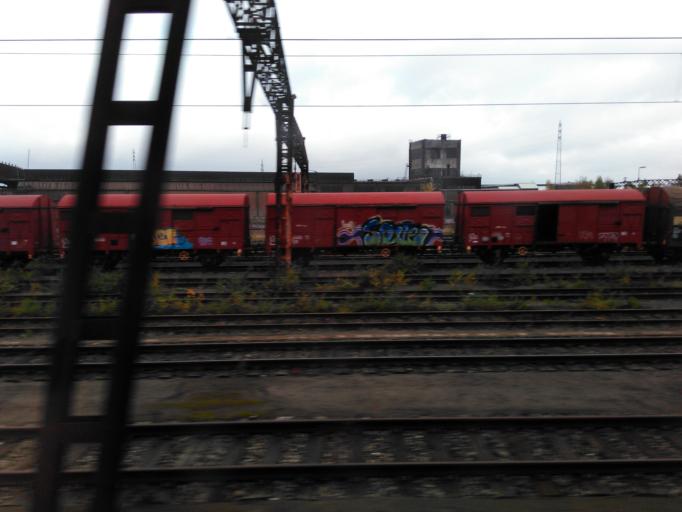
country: LU
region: Luxembourg
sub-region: Canton d'Esch-sur-Alzette
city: Schifflange
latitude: 49.5022
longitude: 5.9967
